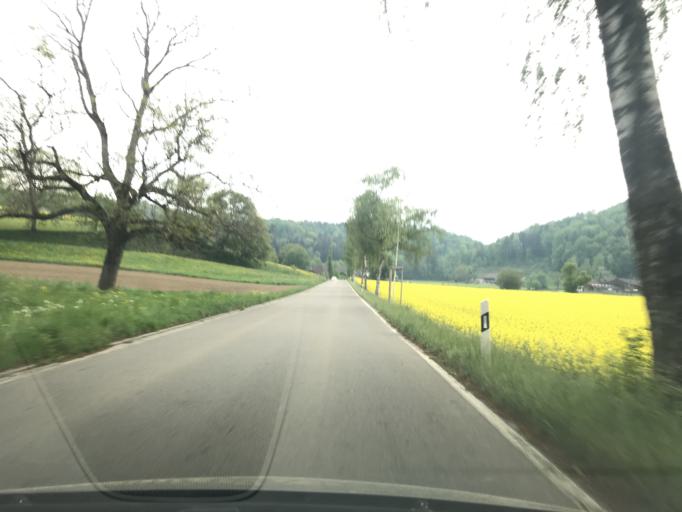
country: CH
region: Zurich
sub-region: Bezirk Winterthur
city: Wuelflingen (Kreis 6) / Niederfeld
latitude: 47.4984
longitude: 8.6731
